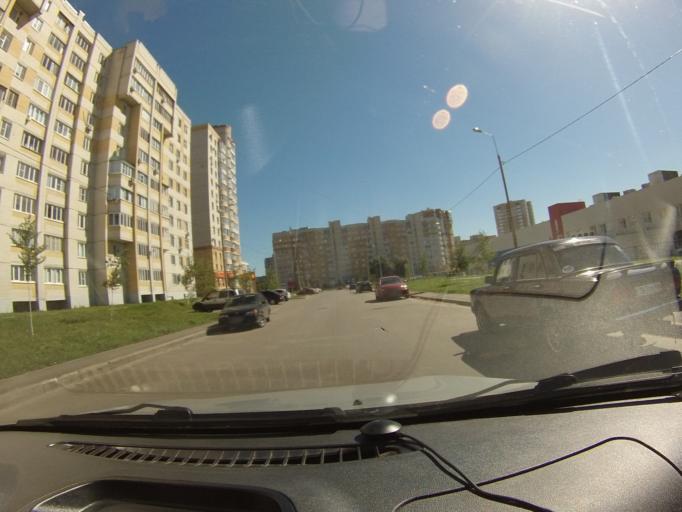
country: RU
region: Tambov
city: Tambov
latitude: 52.7675
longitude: 41.3980
